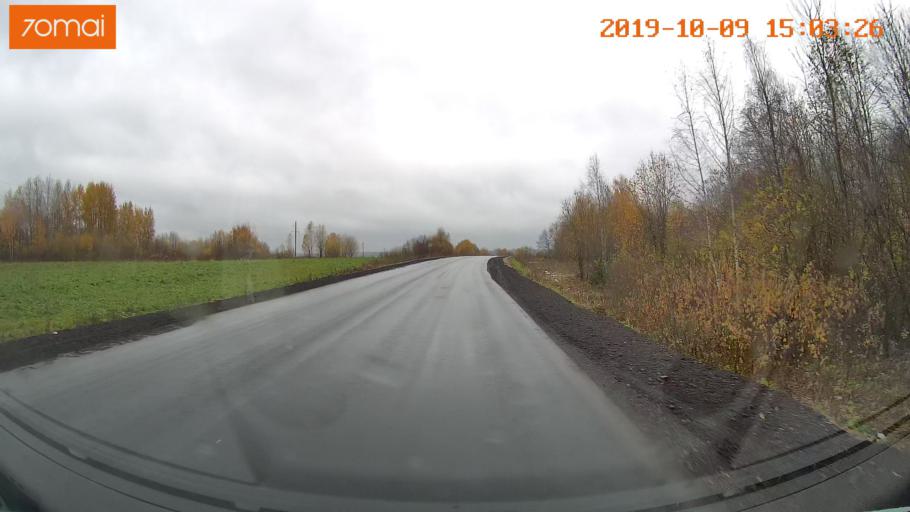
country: RU
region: Kostroma
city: Chistyye Bory
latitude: 58.2713
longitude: 41.6758
